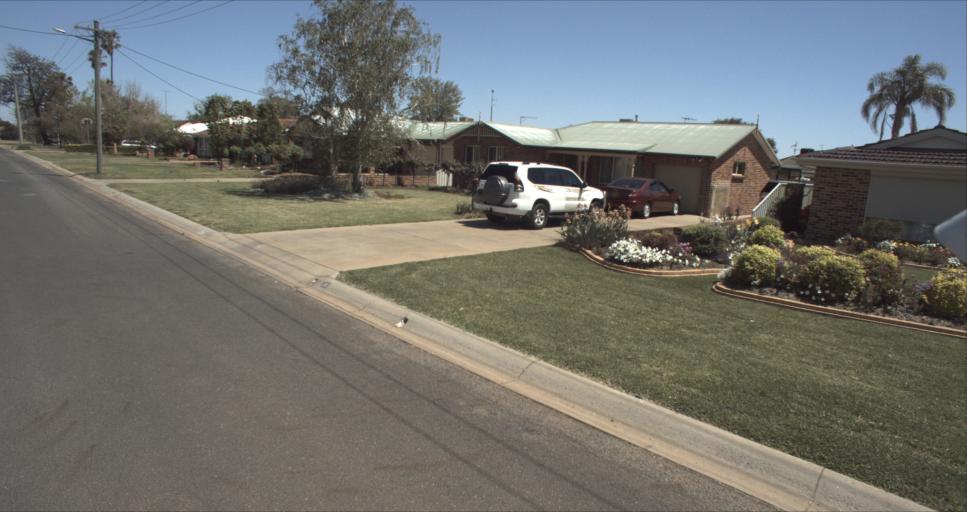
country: AU
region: New South Wales
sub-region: Leeton
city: Leeton
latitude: -34.5439
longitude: 146.4008
